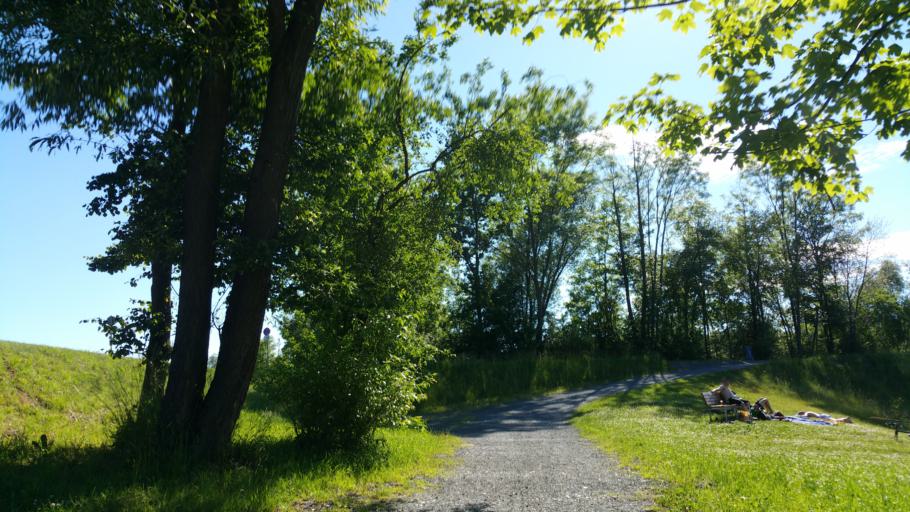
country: DE
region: Bavaria
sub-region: Upper Franconia
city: Schwarzenbach an der Saale
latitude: 50.1892
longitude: 11.9067
